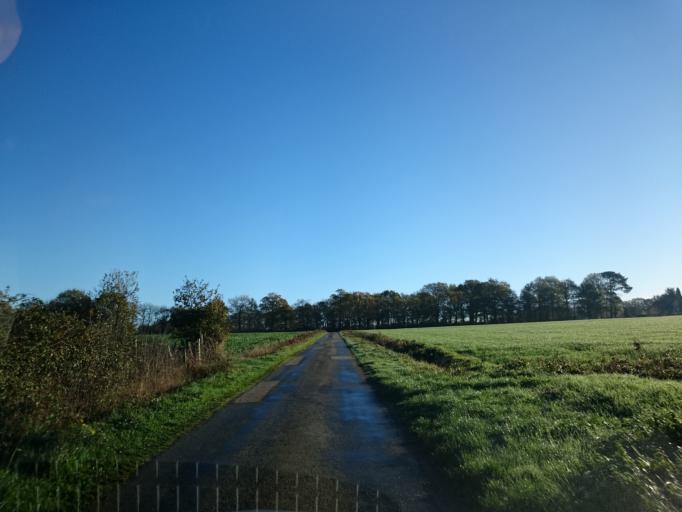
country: FR
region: Brittany
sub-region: Departement d'Ille-et-Vilaine
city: Tresboeuf
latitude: 47.9266
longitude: -1.5585
